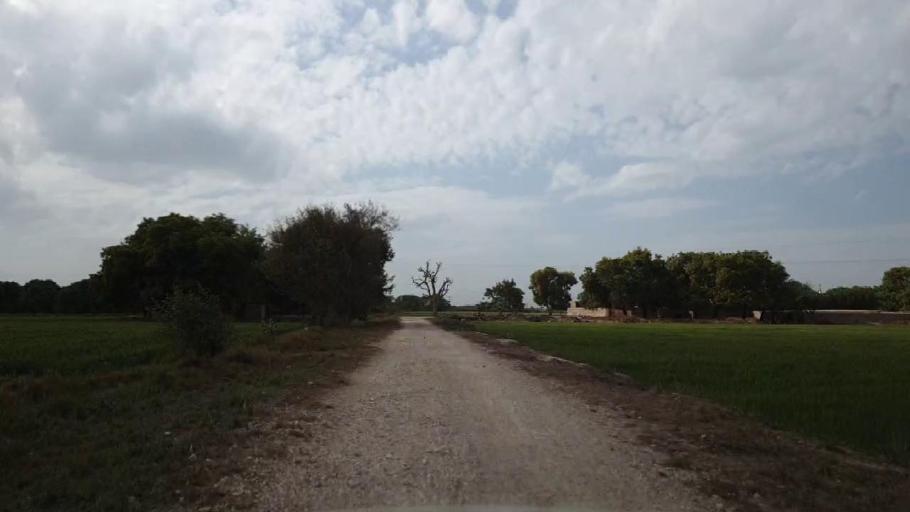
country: PK
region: Sindh
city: Tando Jam
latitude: 25.5386
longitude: 68.5954
